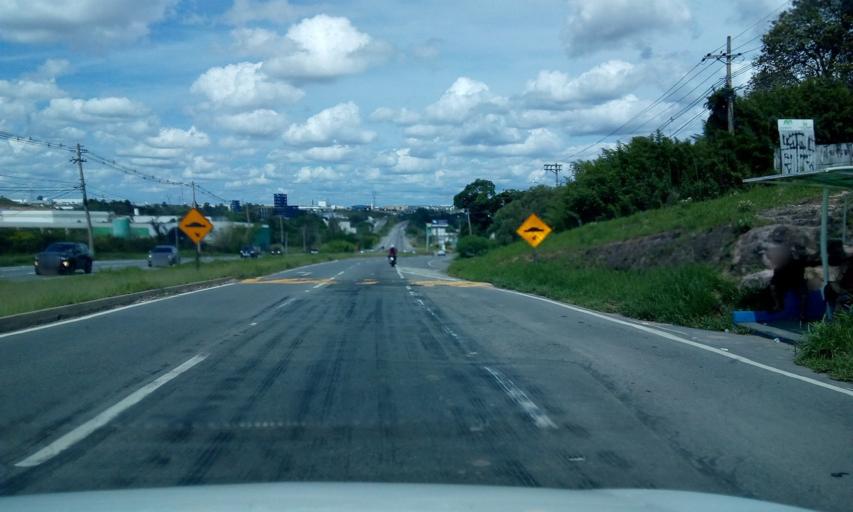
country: BR
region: Sao Paulo
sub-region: Itupeva
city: Itupeva
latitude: -23.1606
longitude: -47.0274
